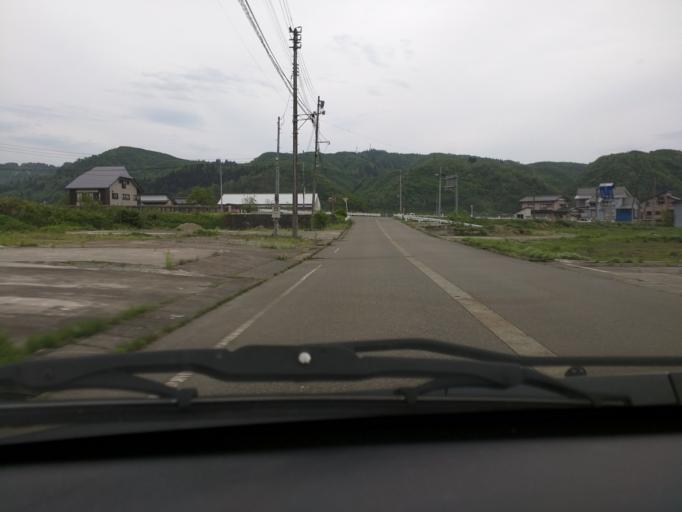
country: JP
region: Niigata
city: Muikamachi
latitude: 37.1943
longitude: 138.9515
